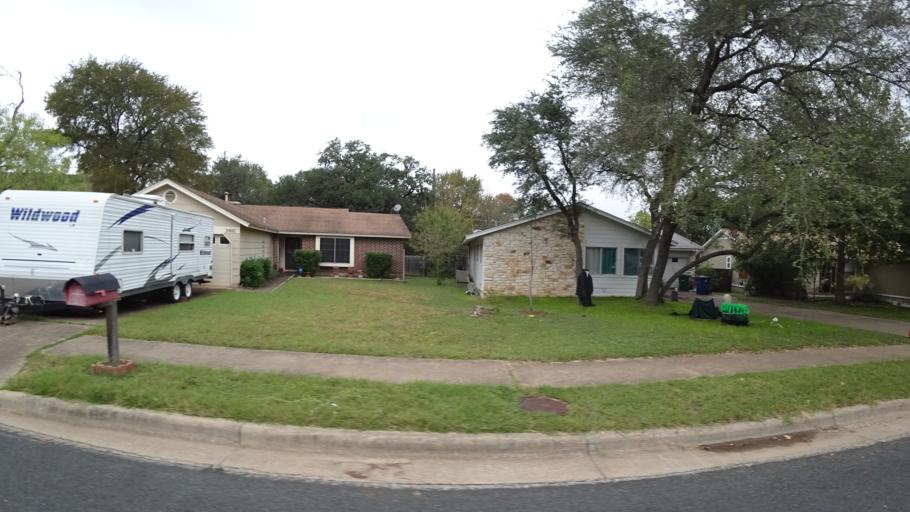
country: US
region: Texas
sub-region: Travis County
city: Shady Hollow
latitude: 30.2096
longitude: -97.8396
